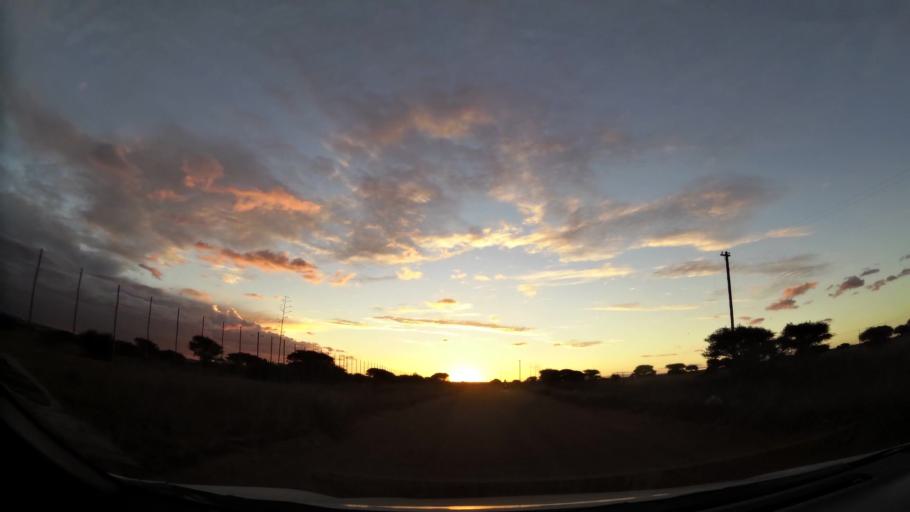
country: ZA
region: Limpopo
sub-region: Capricorn District Municipality
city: Polokwane
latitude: -23.7405
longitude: 29.4520
